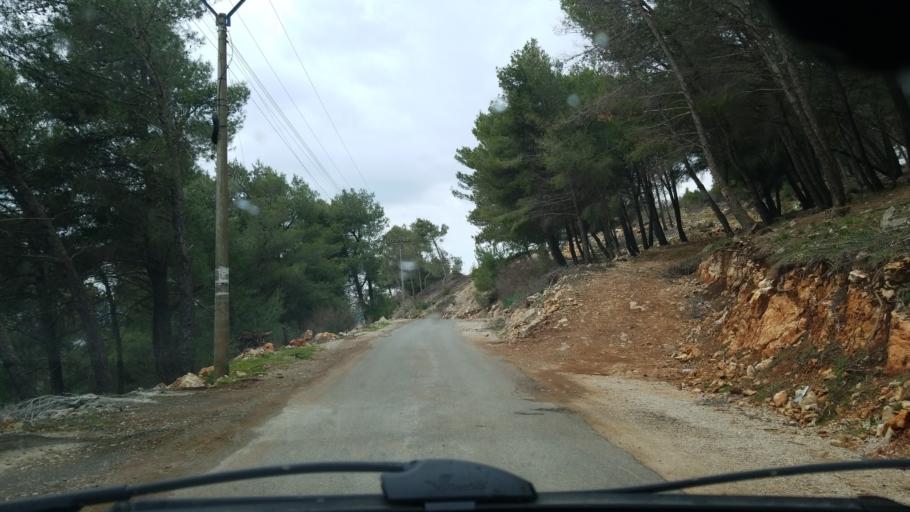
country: AL
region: Lezhe
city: Shengjin
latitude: 41.8146
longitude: 19.5721
